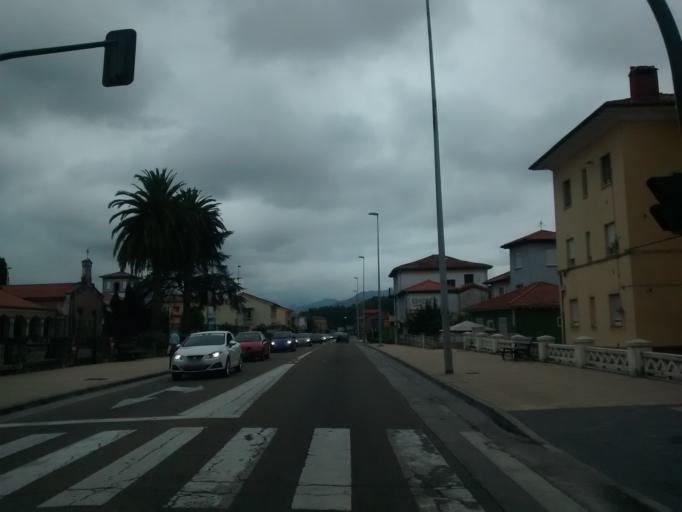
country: ES
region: Cantabria
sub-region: Provincia de Cantabria
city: Torrelavega
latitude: 43.3660
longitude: -4.0446
